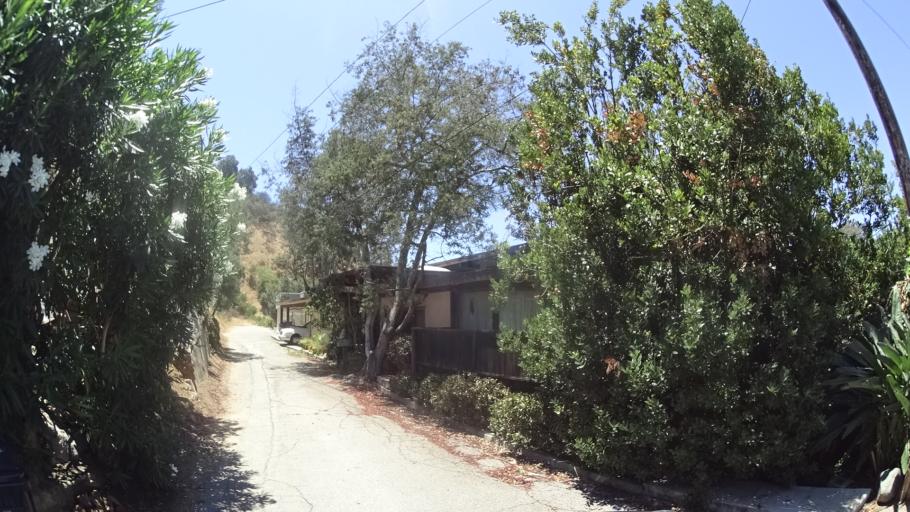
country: US
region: California
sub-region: Los Angeles County
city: West Hollywood
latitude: 34.1169
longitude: -118.3722
